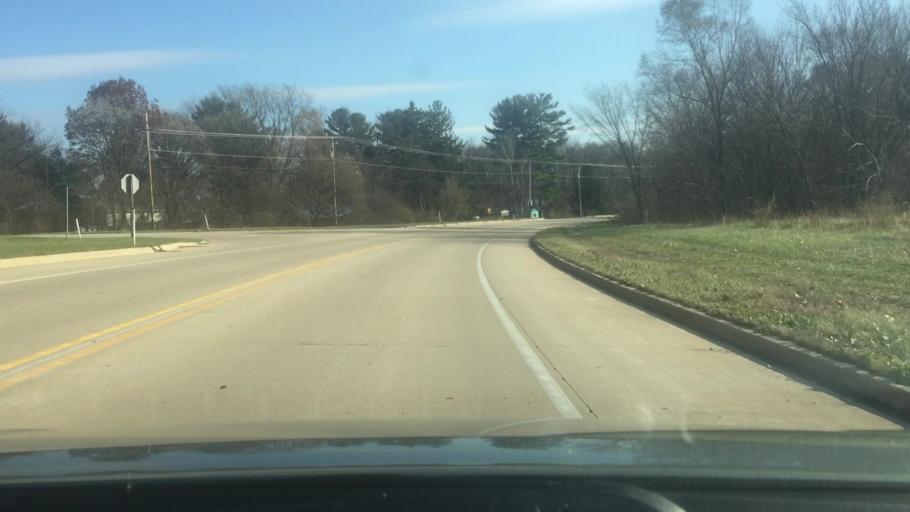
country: US
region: Wisconsin
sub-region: Jefferson County
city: Cambridge
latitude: 42.9992
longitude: -89.0037
